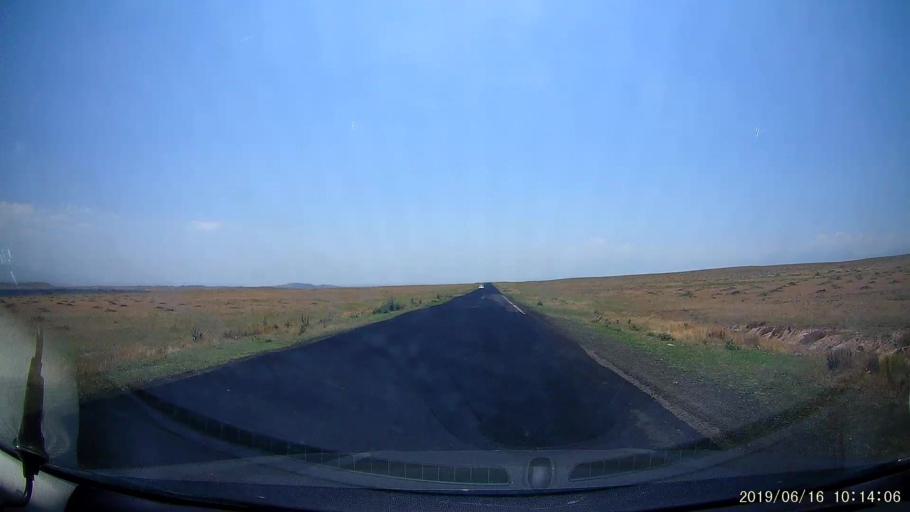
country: TR
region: Igdir
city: Tuzluca
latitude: 40.1879
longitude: 43.6557
